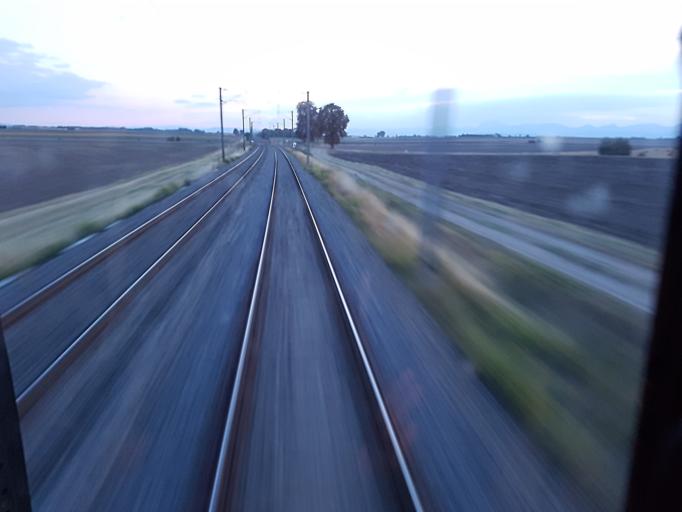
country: FR
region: Auvergne
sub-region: Departement du Puy-de-Dome
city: Ennezat
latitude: 45.9525
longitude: 3.2474
